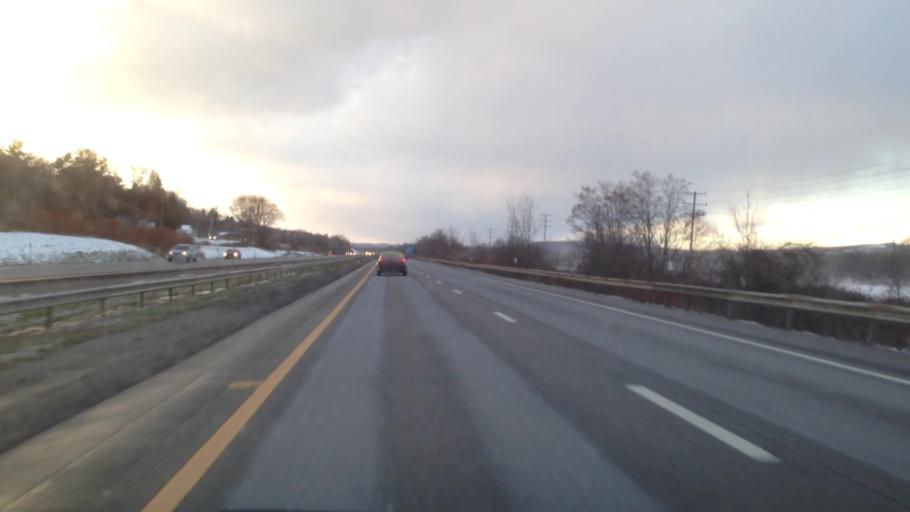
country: US
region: New York
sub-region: Herkimer County
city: Herkimer
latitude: 43.0140
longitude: -74.9319
